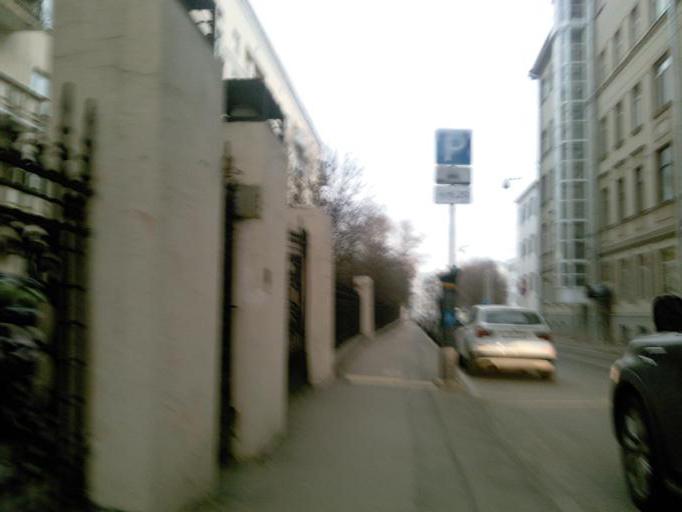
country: RU
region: Moskovskaya
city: Dorogomilovo
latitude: 55.7398
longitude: 37.5900
